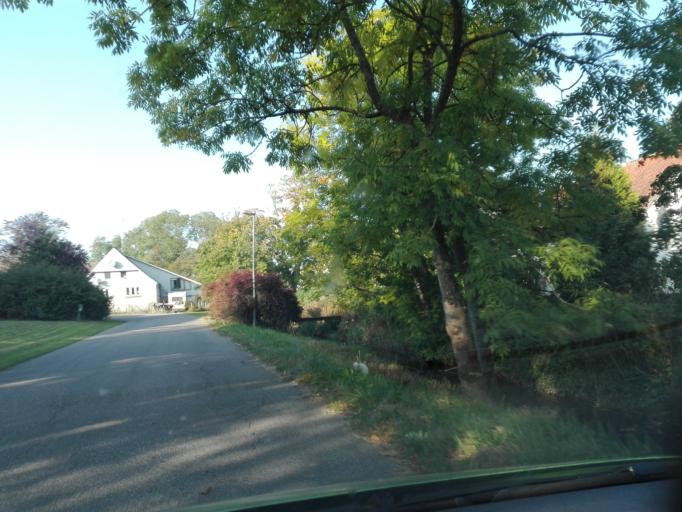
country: DK
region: Central Jutland
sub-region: Odder Kommune
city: Odder
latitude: 55.8911
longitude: 10.1656
